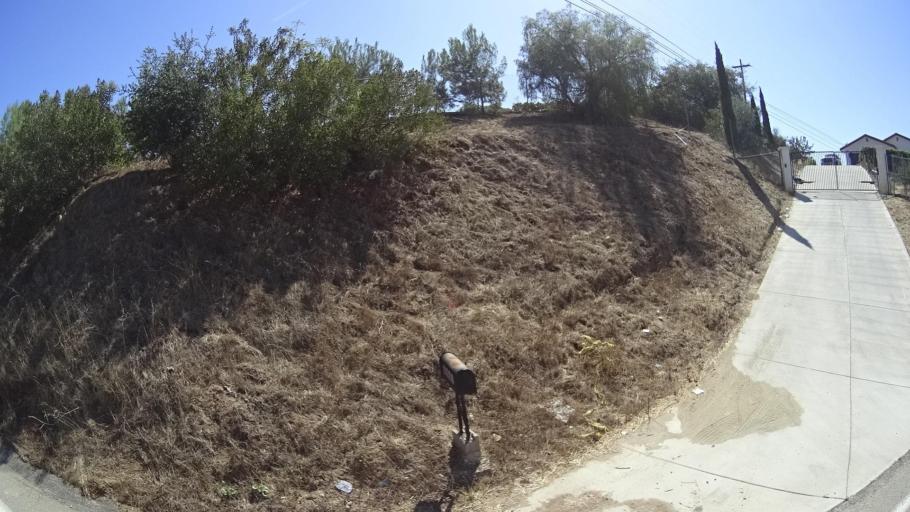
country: US
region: California
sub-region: San Diego County
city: Bonsall
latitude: 33.2930
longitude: -117.1897
